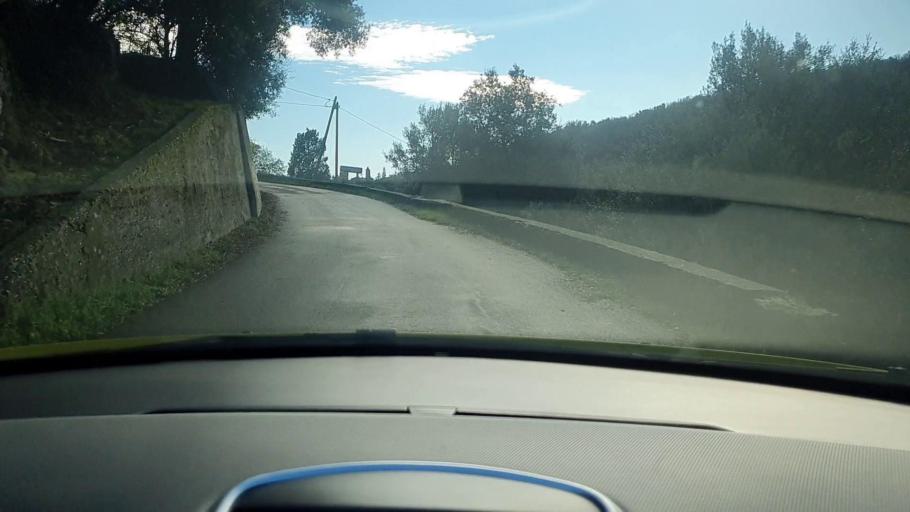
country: FR
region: Languedoc-Roussillon
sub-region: Departement du Gard
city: Valleraugue
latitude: 44.1708
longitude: 3.6478
